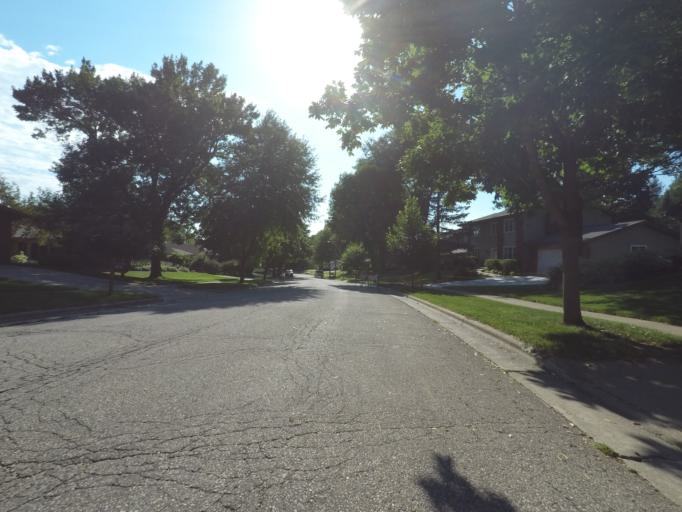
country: US
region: Wisconsin
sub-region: Dane County
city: Middleton
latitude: 43.0693
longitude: -89.5063
